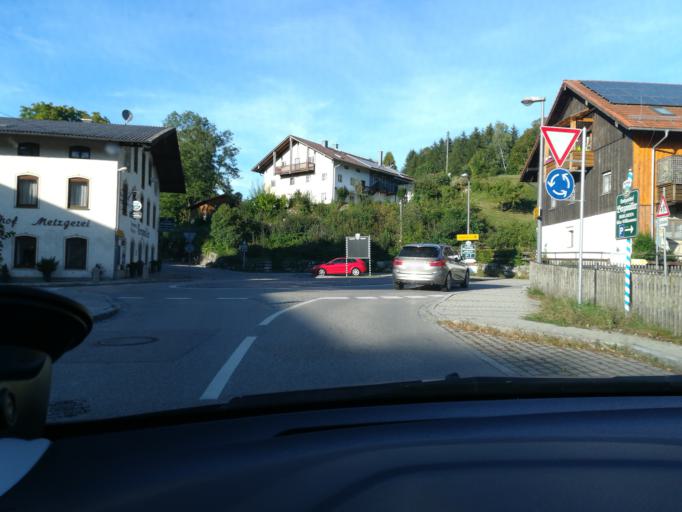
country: DE
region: Bavaria
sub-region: Upper Bavaria
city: Feldkirchen-Westerham
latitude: 47.9405
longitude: 11.8622
